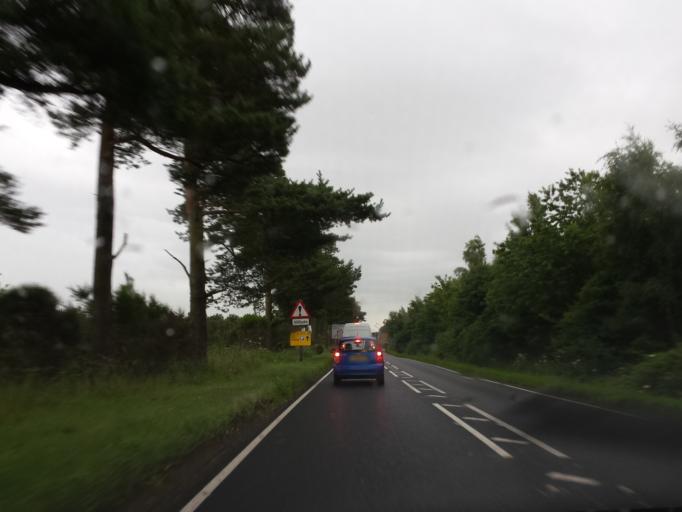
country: GB
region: Scotland
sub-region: Fife
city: Balmullo
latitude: 56.3964
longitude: -2.9083
